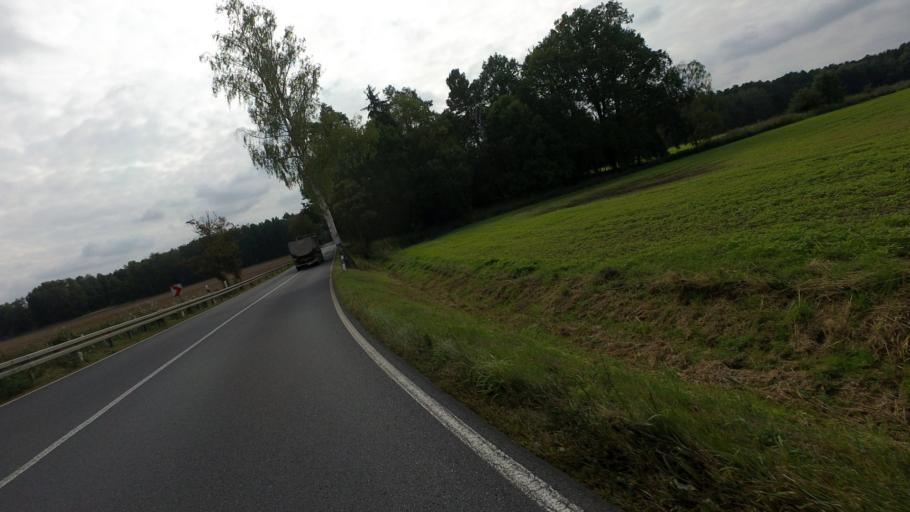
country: DE
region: Brandenburg
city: Kasel-Golzig
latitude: 51.8948
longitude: 13.6841
